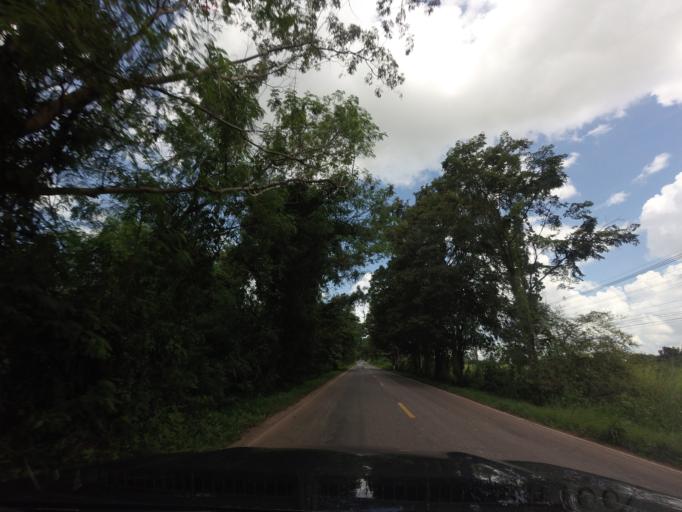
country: TH
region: Changwat Udon Thani
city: Phibun Rak
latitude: 17.6481
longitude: 103.1287
